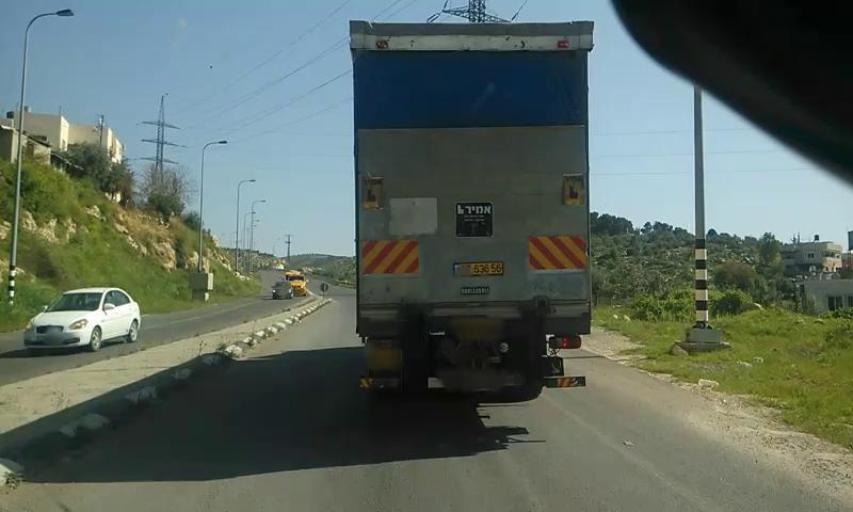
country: PS
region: West Bank
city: Idhna
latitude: 31.5701
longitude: 34.9858
